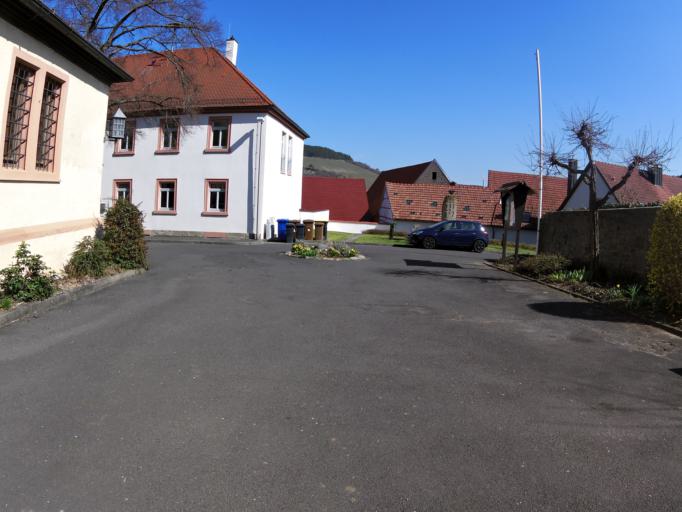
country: DE
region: Bavaria
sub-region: Regierungsbezirk Unterfranken
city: Erlabrunn
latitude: 49.8599
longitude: 9.8070
